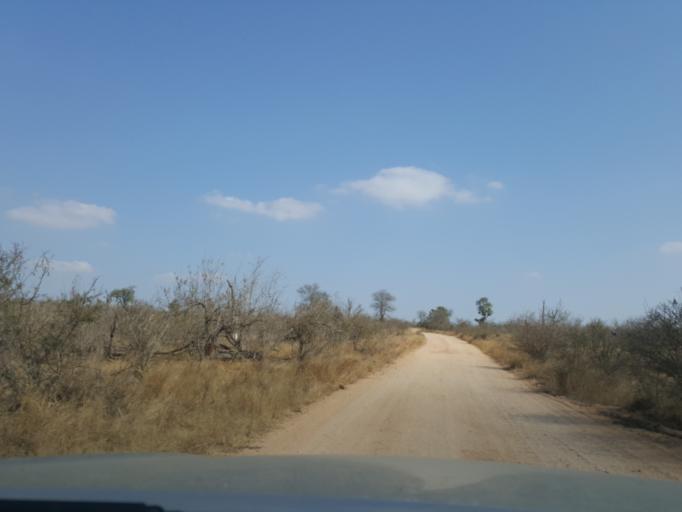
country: ZA
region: Mpumalanga
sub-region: Ehlanzeni District
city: Komatipoort
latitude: -25.3003
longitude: 31.7572
